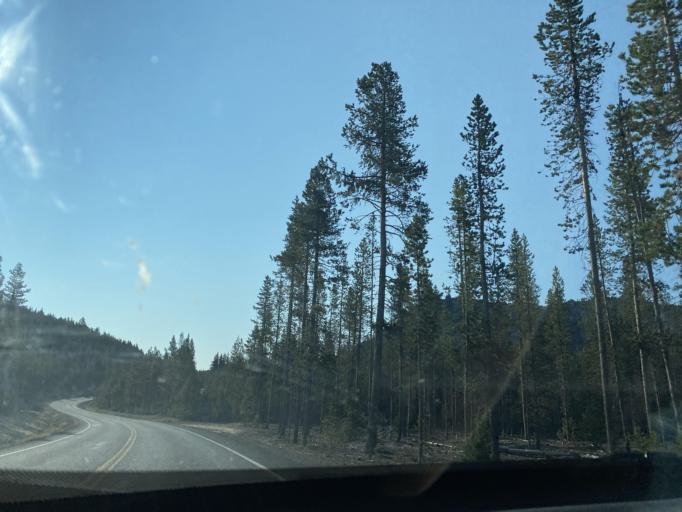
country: US
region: Oregon
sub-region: Deschutes County
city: Three Rivers
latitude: 43.7076
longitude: -121.2695
